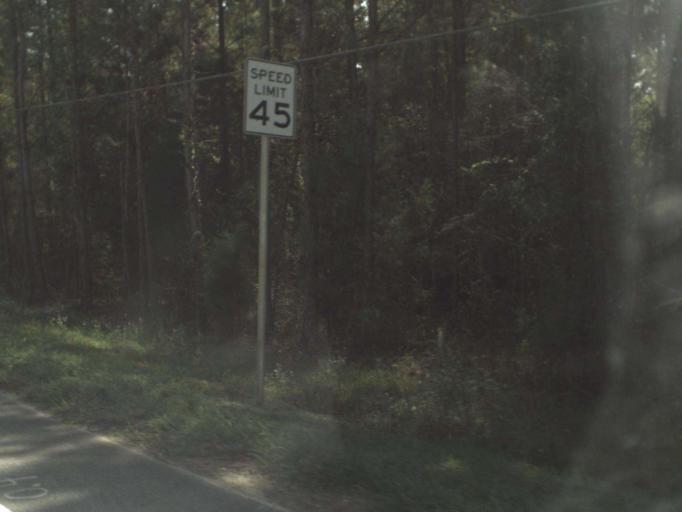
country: US
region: Florida
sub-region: Jackson County
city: Marianna
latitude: 30.7899
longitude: -85.2620
